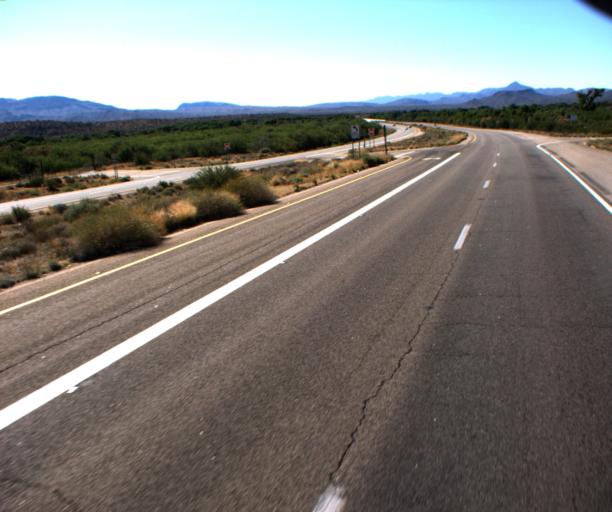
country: US
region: Arizona
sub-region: Yavapai County
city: Bagdad
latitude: 34.6706
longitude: -113.5881
